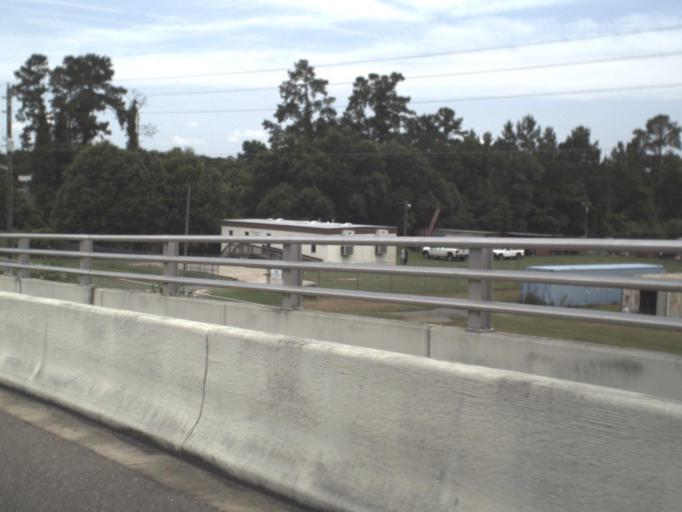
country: US
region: Florida
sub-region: Alachua County
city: Hawthorne
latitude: 29.5964
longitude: -82.0889
